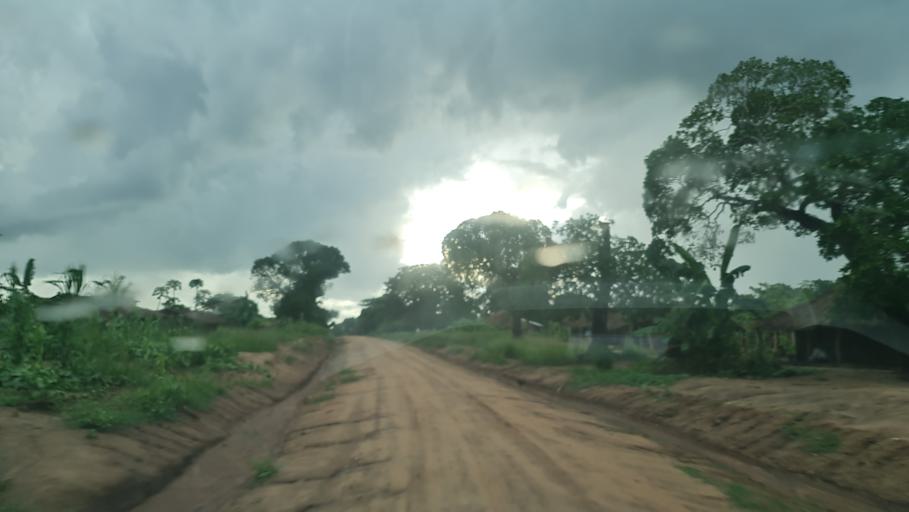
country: MZ
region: Nampula
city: Nacala
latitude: -13.9887
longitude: 40.3759
